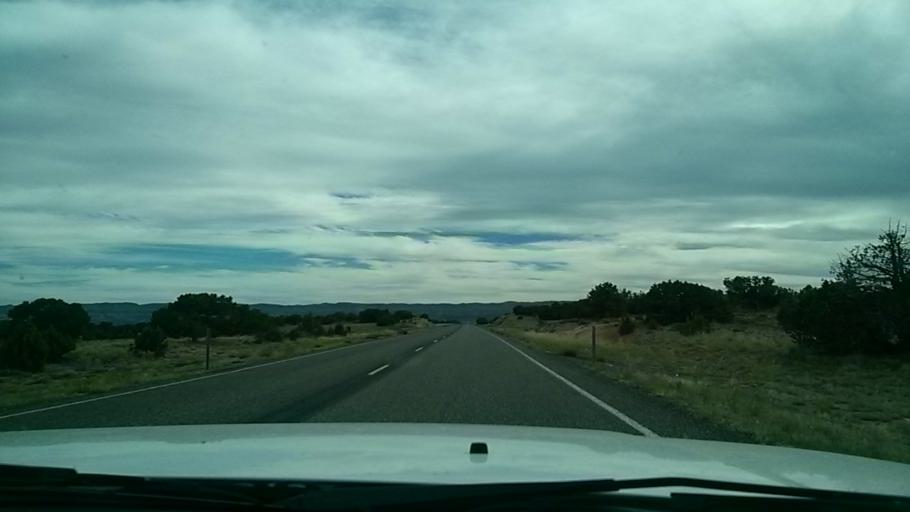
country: US
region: Utah
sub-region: Wayne County
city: Loa
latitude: 37.7454
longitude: -111.4980
